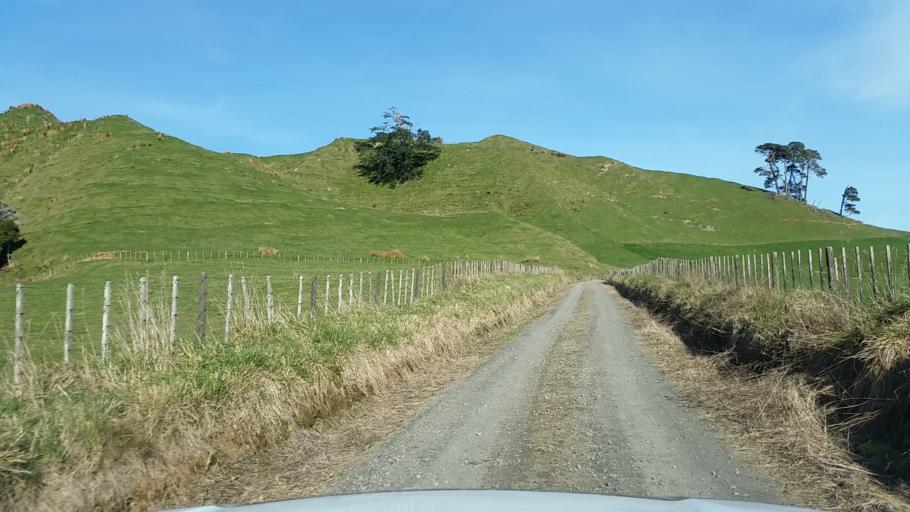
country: NZ
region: Taranaki
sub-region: South Taranaki District
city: Eltham
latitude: -39.3110
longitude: 174.5495
